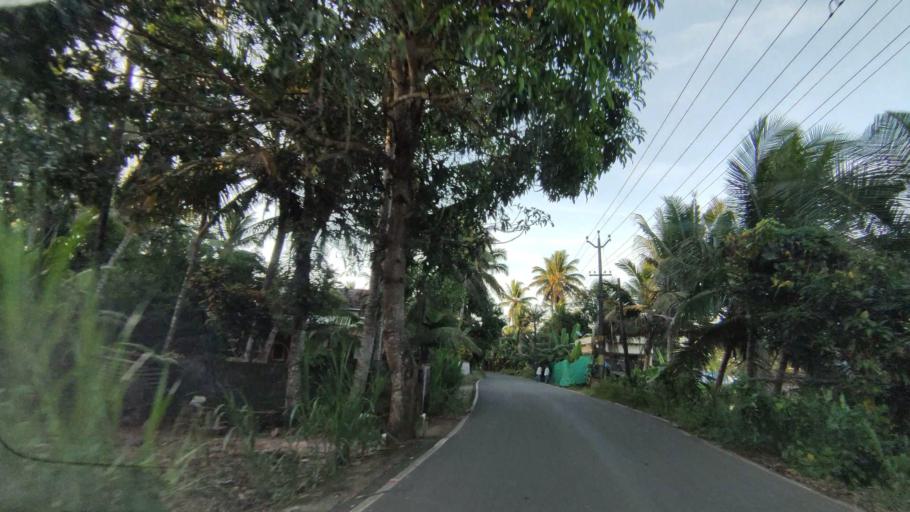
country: IN
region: Kerala
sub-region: Kottayam
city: Kottayam
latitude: 9.6265
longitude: 76.4874
